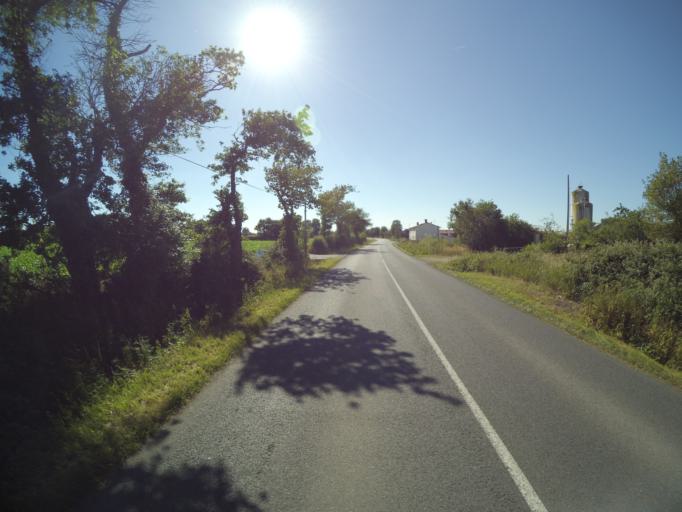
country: FR
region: Pays de la Loire
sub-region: Departement de la Vendee
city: Saint-Georges-de-Montaigu
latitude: 46.9657
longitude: -1.2829
